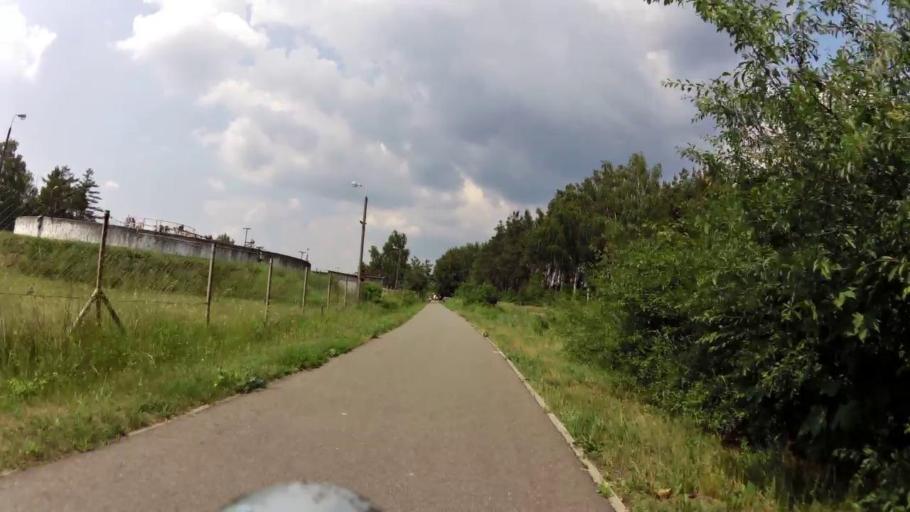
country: PL
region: Kujawsko-Pomorskie
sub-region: Powiat bydgoski
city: Koronowo
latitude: 53.3011
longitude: 17.9465
